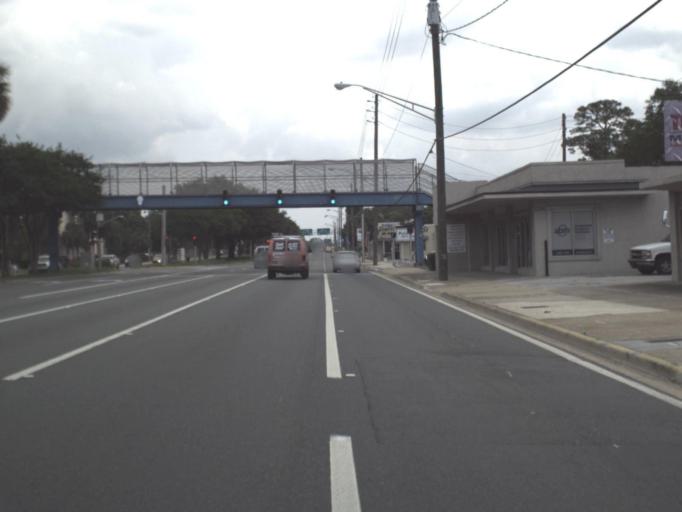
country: US
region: Florida
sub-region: Duval County
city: Jacksonville
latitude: 30.3074
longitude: -81.6425
